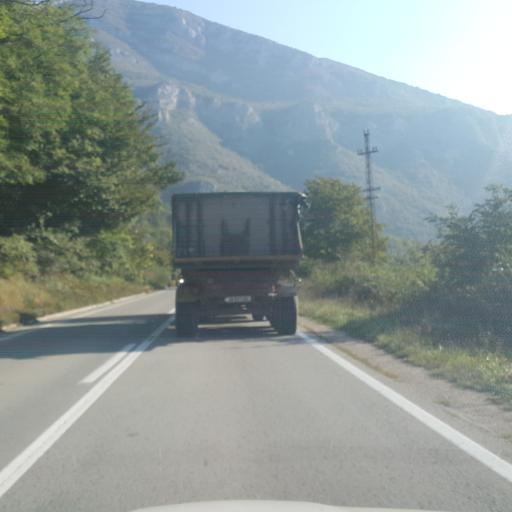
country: RS
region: Central Serbia
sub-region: Nisavski Okrug
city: Svrljig
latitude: 43.3339
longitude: 22.1193
